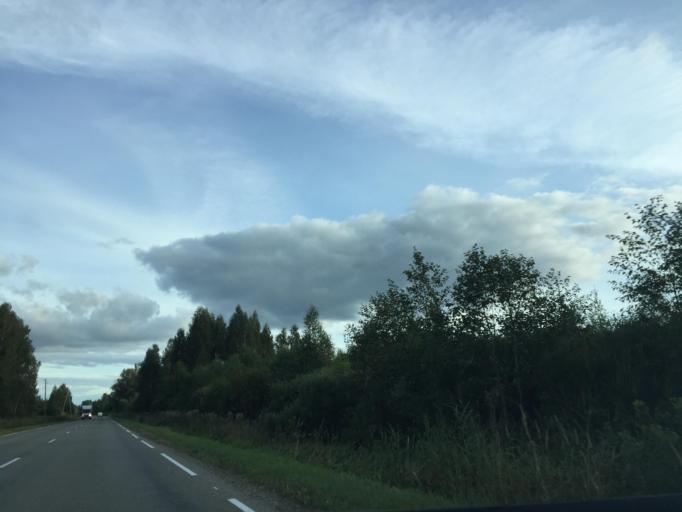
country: LV
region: Nereta
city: Nereta
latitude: 56.3069
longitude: 25.1015
